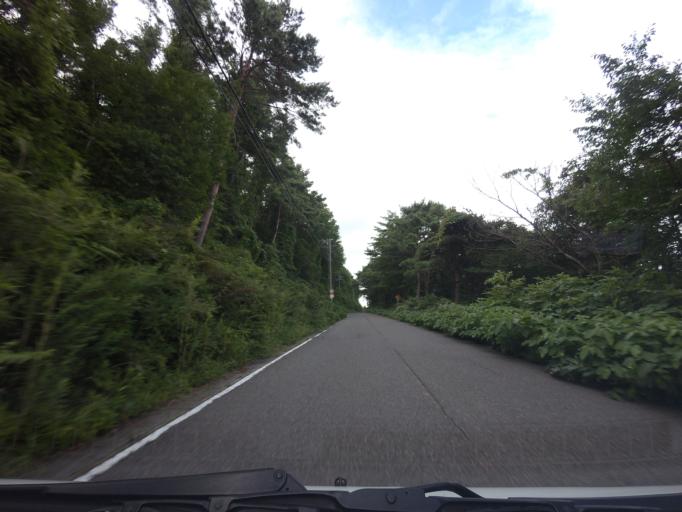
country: JP
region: Fukushima
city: Nihommatsu
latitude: 37.6190
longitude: 140.3390
